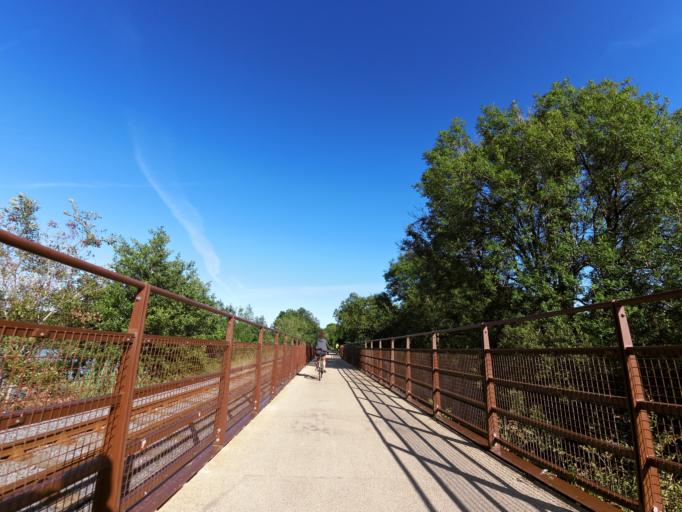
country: IE
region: Leinster
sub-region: Kilkenny
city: Mooncoin
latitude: 52.2463
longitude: -7.2309
